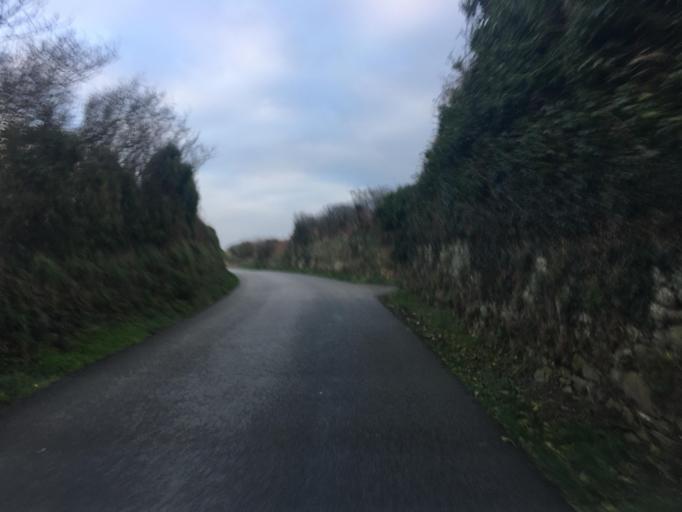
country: FR
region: Lower Normandy
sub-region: Departement de la Manche
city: Beaumont-Hague
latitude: 49.7117
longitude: -1.9275
